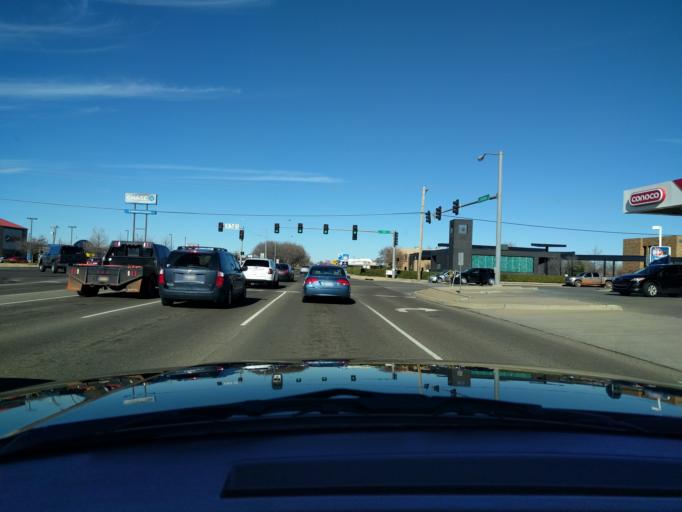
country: US
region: Oklahoma
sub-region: Oklahoma County
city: Edmond
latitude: 35.6379
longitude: -97.4833
